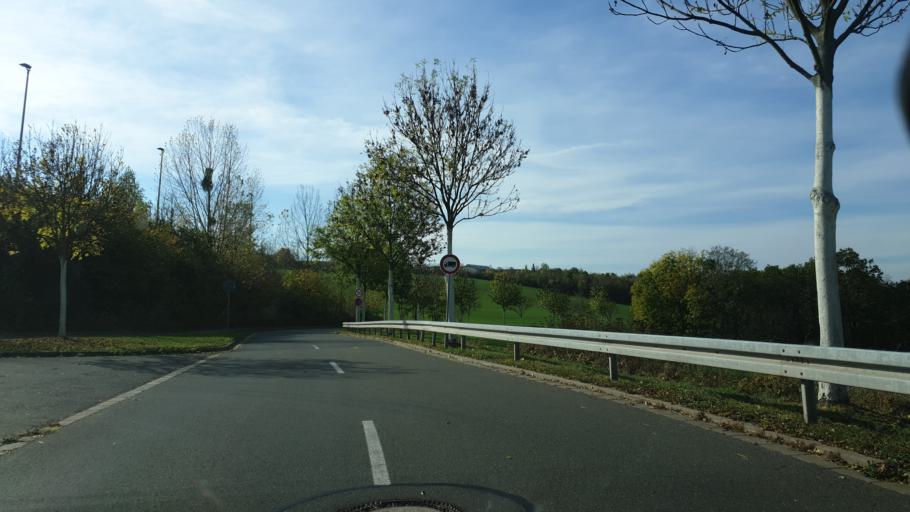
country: DE
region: Thuringia
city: Gera
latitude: 50.9059
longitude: 12.1054
